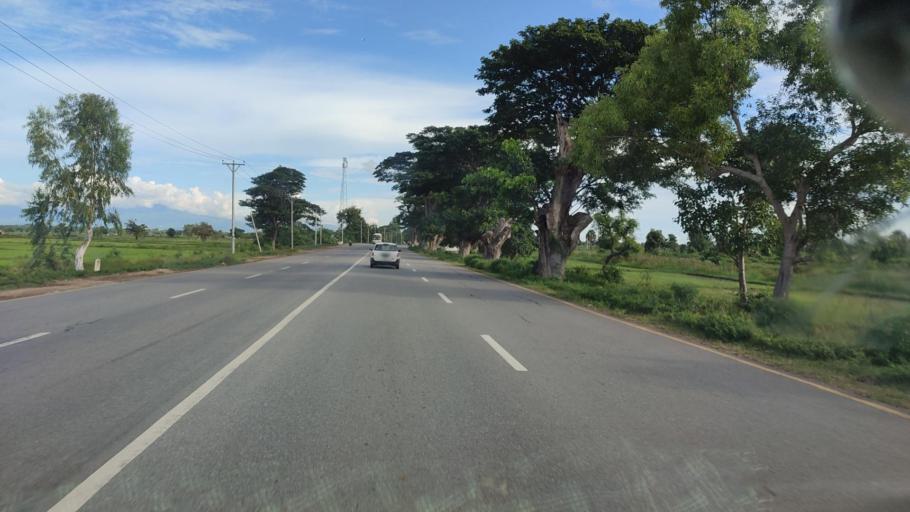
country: MM
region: Mandalay
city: Yamethin
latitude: 20.1984
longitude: 96.1823
